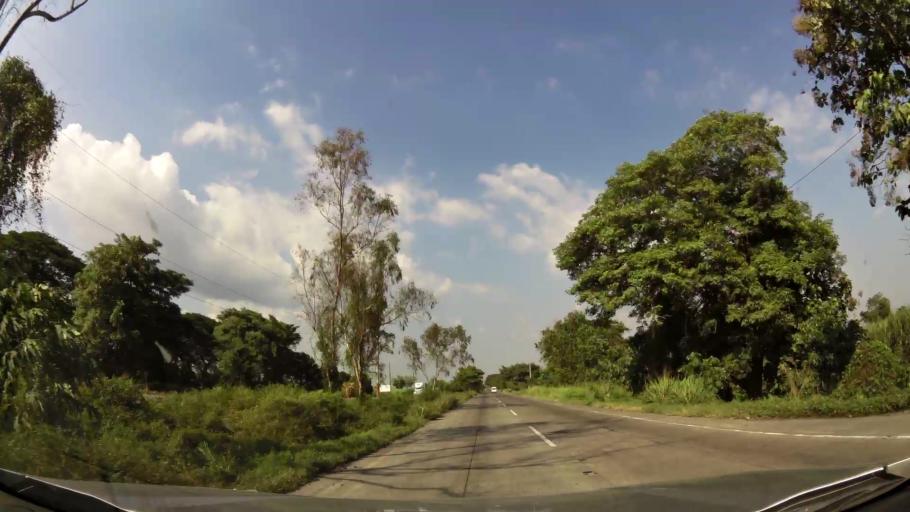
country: GT
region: Escuintla
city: Puerto San Jose
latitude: 14.0127
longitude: -90.7847
